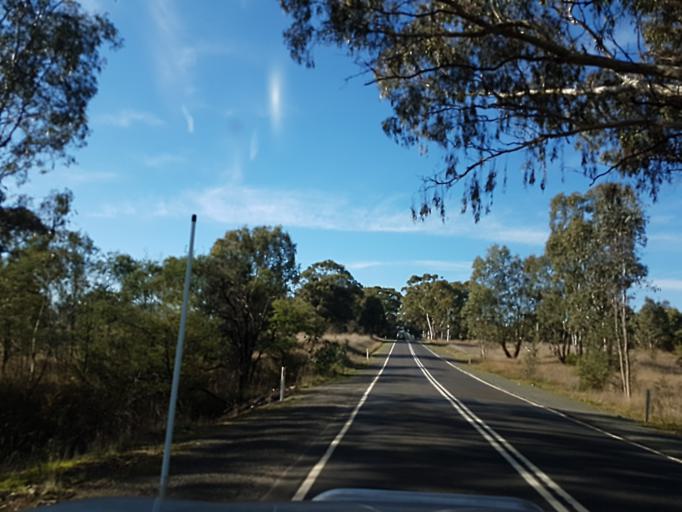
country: AU
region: Victoria
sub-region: Murrindindi
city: Alexandra
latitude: -37.1481
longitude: 145.6093
